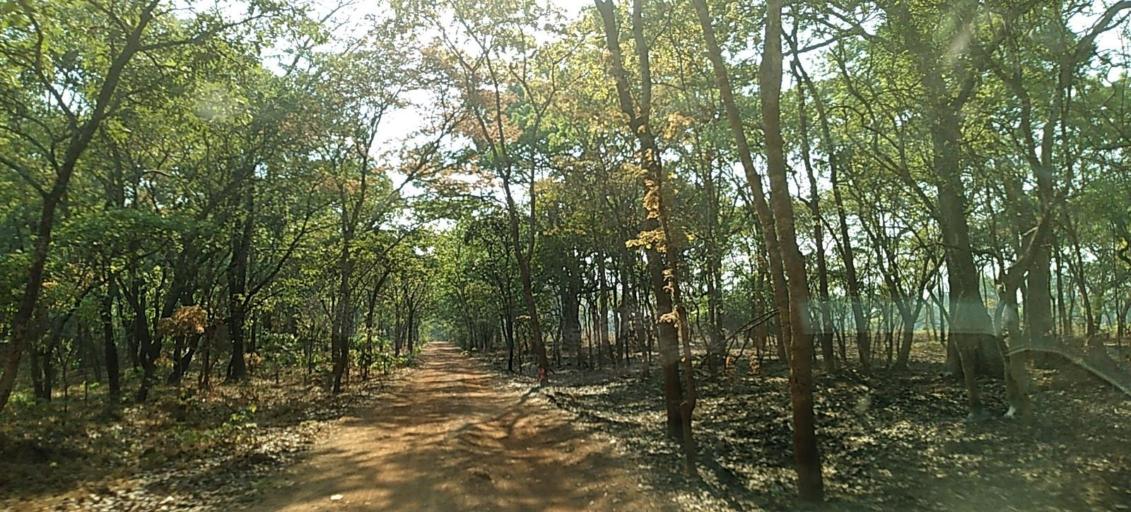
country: ZM
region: Copperbelt
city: Kalulushi
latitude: -13.0054
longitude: 27.7473
